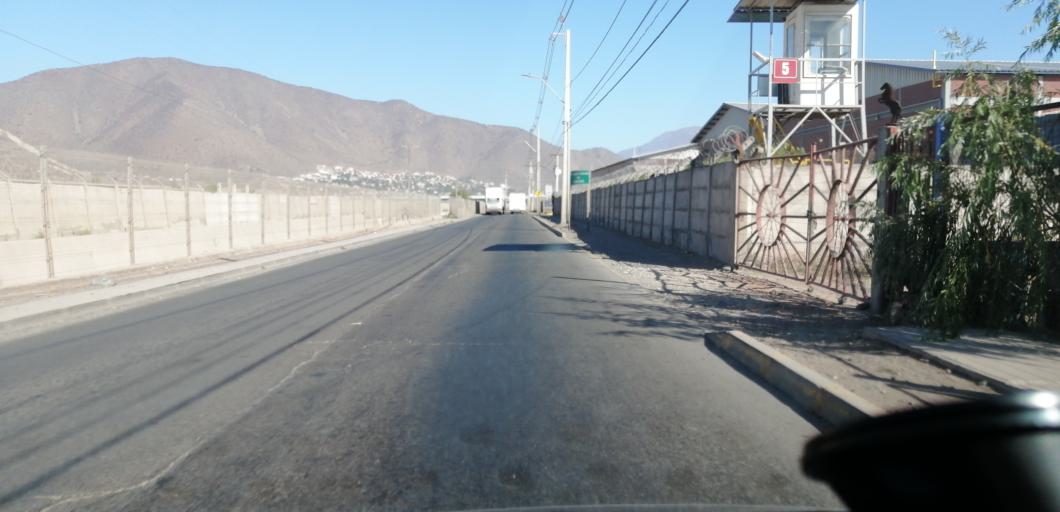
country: CL
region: Santiago Metropolitan
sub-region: Provincia de Santiago
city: Lo Prado
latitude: -33.4566
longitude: -70.7941
